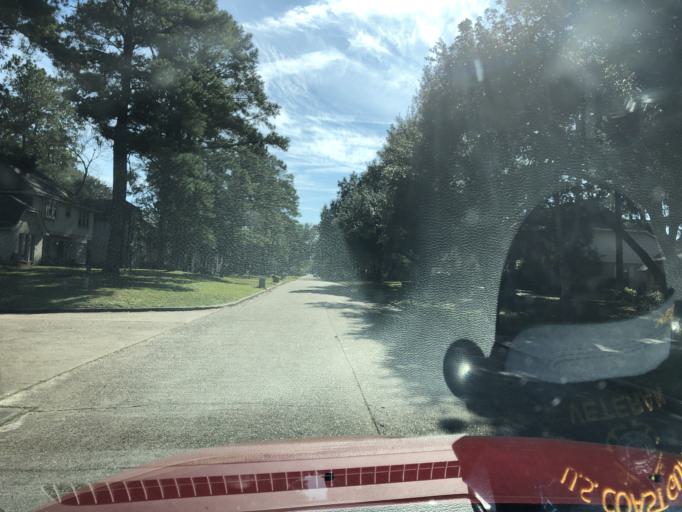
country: US
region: Texas
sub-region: Harris County
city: Tomball
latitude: 30.0269
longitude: -95.5539
